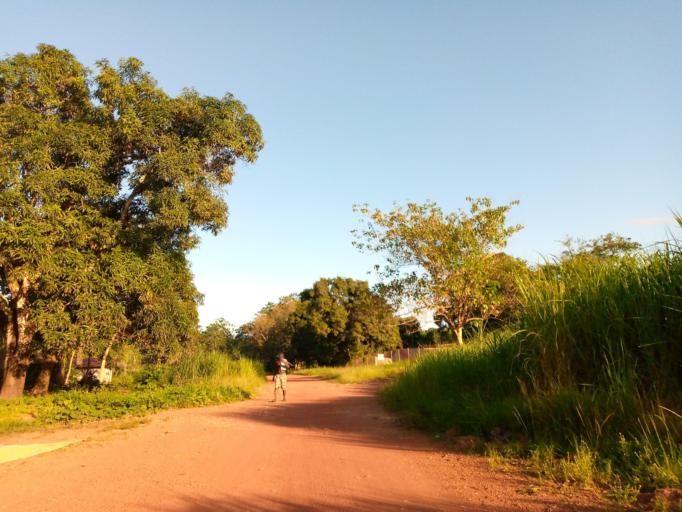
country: SL
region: Northern Province
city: Yonibana
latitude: 8.4506
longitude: -12.2440
